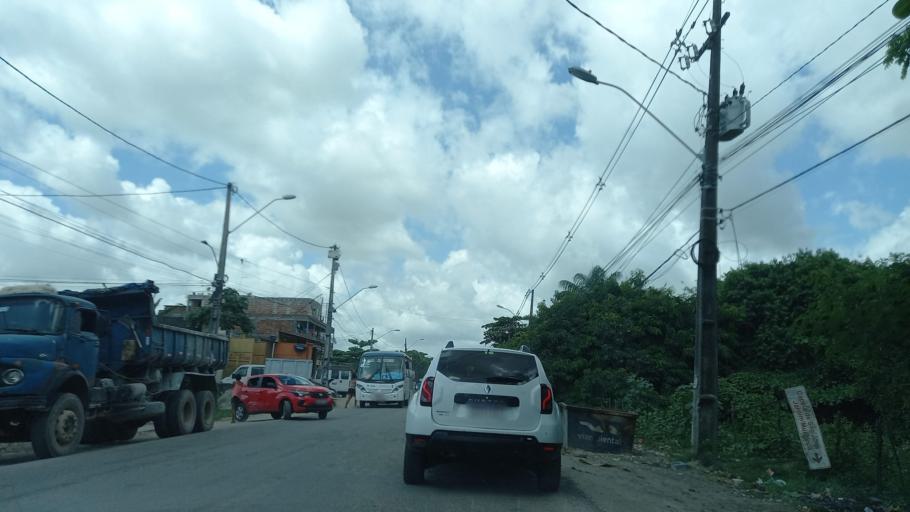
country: BR
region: Pernambuco
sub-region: Jaboatao Dos Guararapes
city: Jaboatao
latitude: -8.1577
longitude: -34.9718
